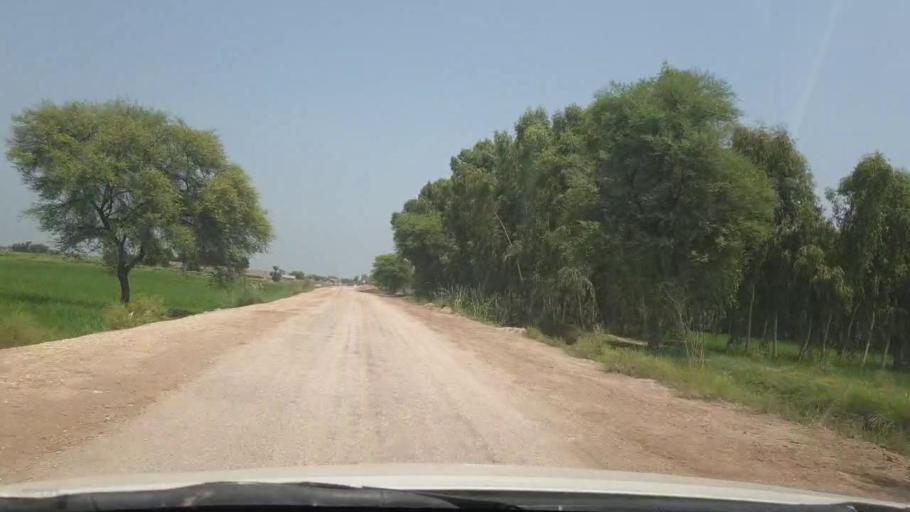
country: PK
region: Sindh
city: Rustam jo Goth
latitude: 28.0290
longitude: 68.7796
